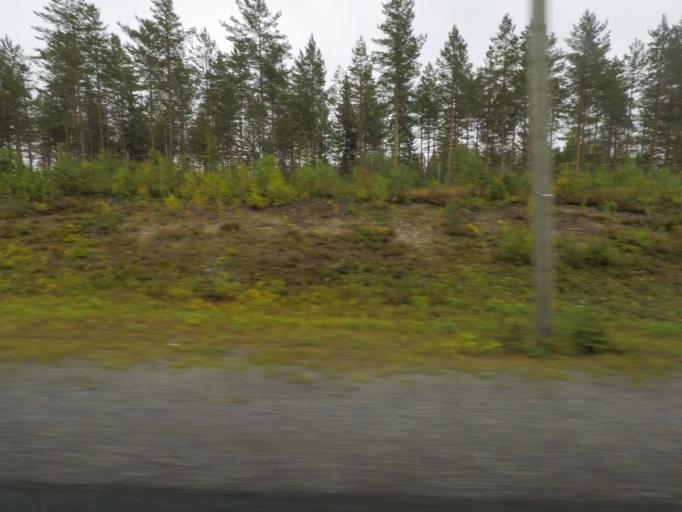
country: FI
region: Northern Savo
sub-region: Kuopio
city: Kuopio
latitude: 62.7596
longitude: 27.5805
